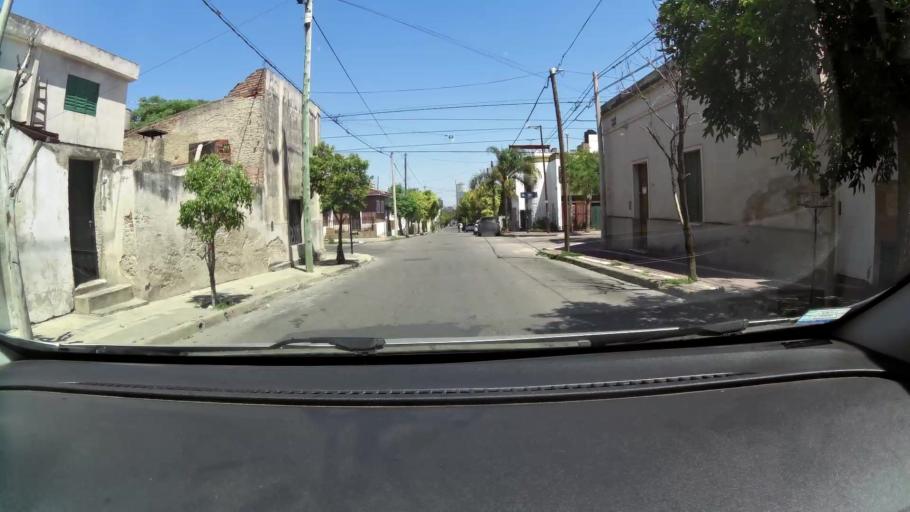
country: AR
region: Cordoba
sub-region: Departamento de Capital
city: Cordoba
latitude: -31.3940
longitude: -64.1984
